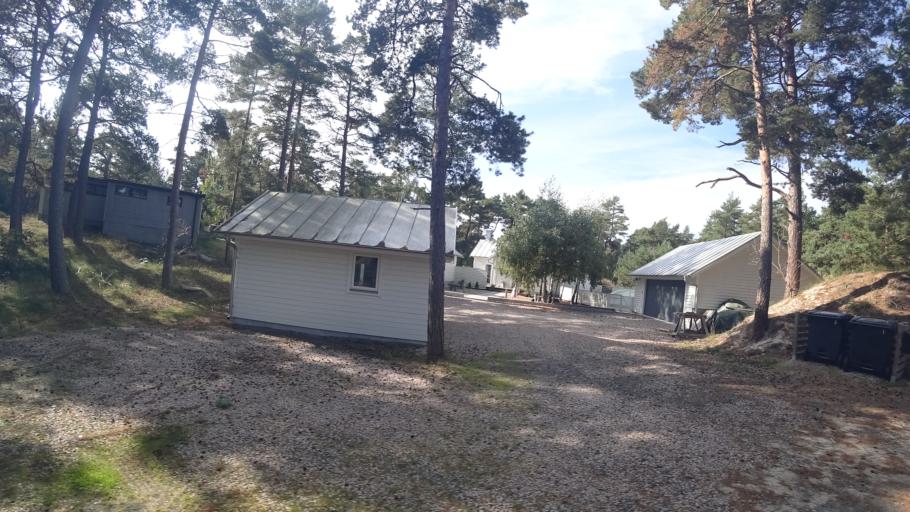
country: SE
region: Skane
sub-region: Kristianstads Kommun
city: Ahus
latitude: 55.9152
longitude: 14.3016
